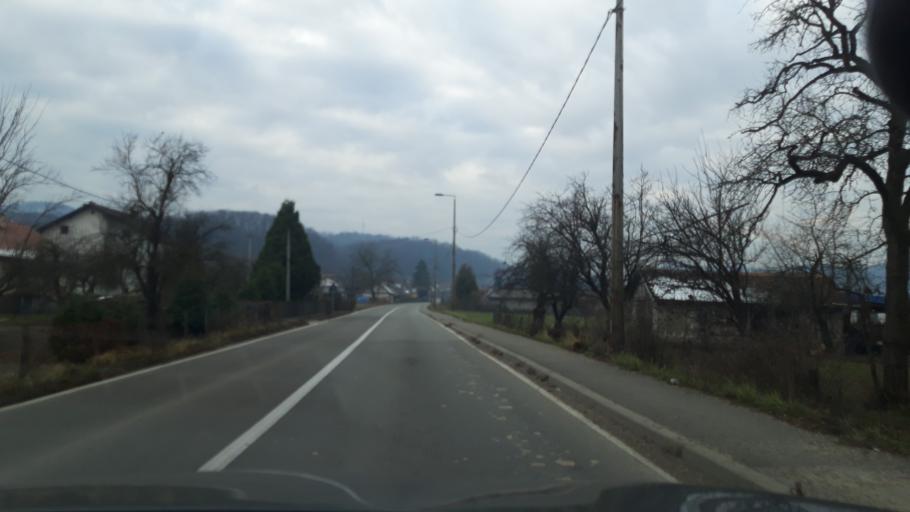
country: BA
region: Republika Srpska
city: Zvornik
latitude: 44.4103
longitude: 19.1462
